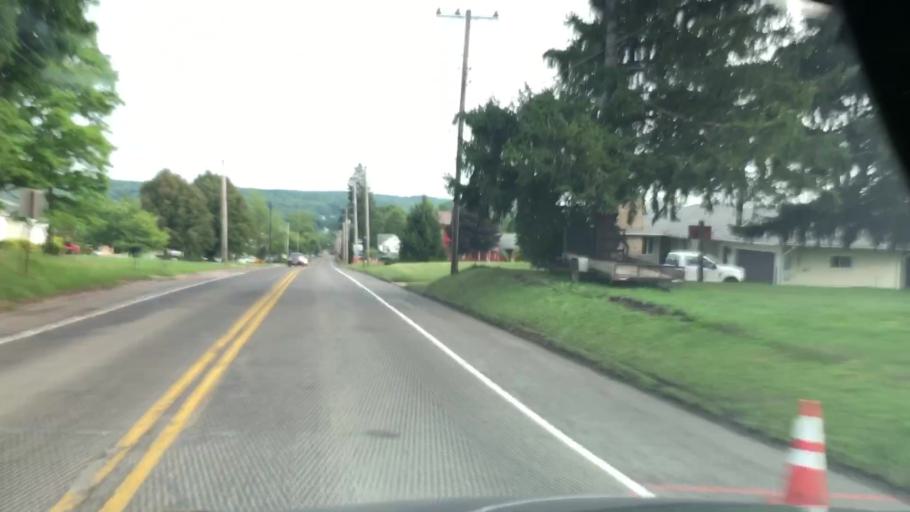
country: US
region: Pennsylvania
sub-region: Crawford County
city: Titusville
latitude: 41.7429
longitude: -79.7657
